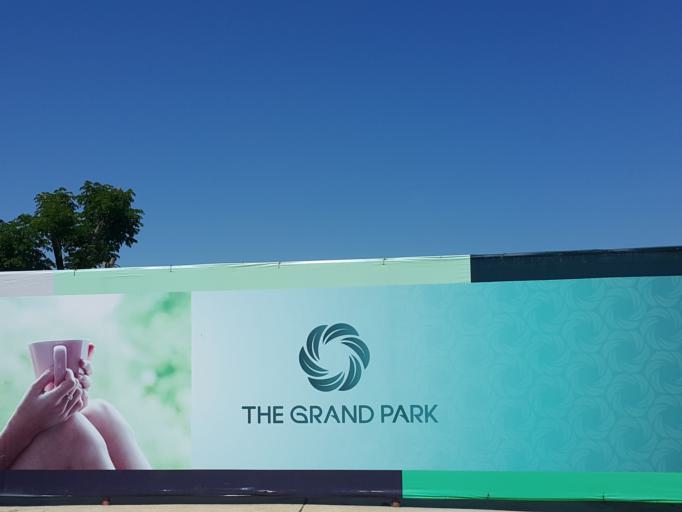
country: TH
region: Chiang Mai
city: San Sai
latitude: 18.8203
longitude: 99.0495
